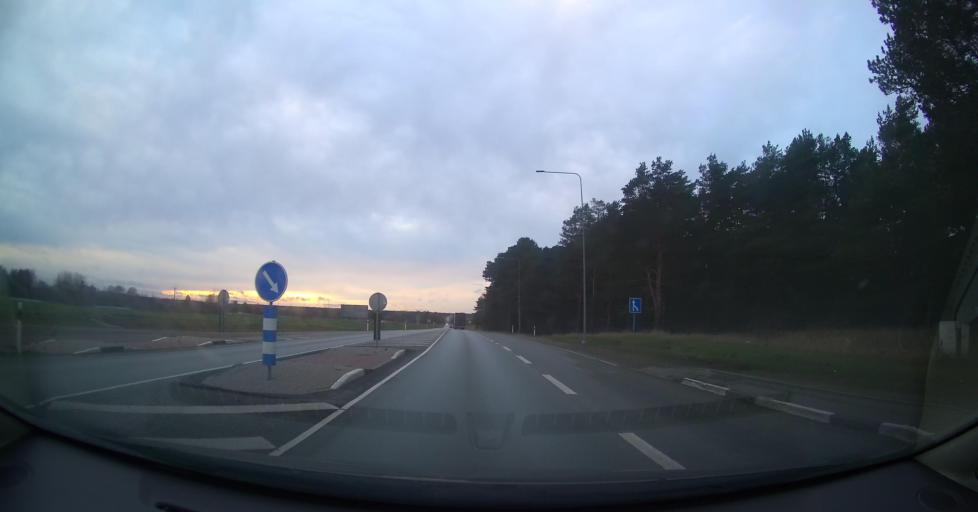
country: EE
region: Ida-Virumaa
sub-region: Puessi linn
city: Pussi
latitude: 59.4127
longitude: 27.0260
